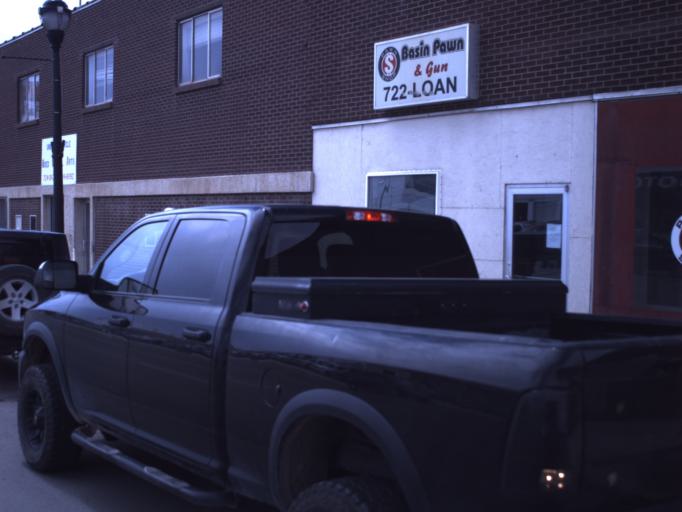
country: US
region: Utah
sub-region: Duchesne County
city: Roosevelt
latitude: 40.2975
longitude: -109.9889
